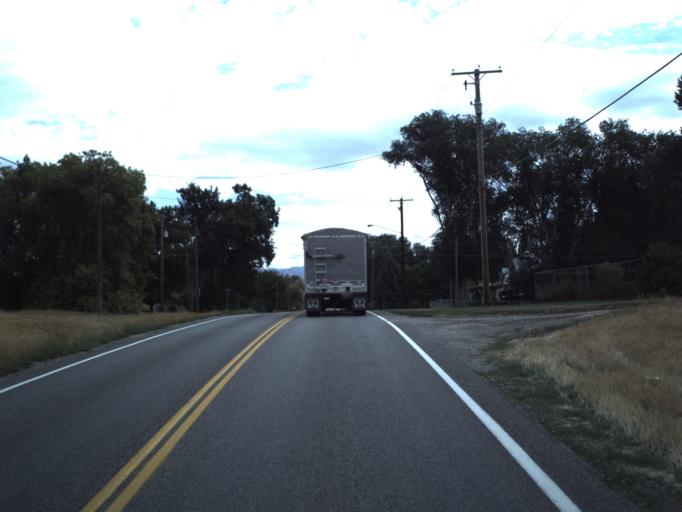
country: US
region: Utah
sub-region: Cache County
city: Benson
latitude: 41.8625
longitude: -111.9952
